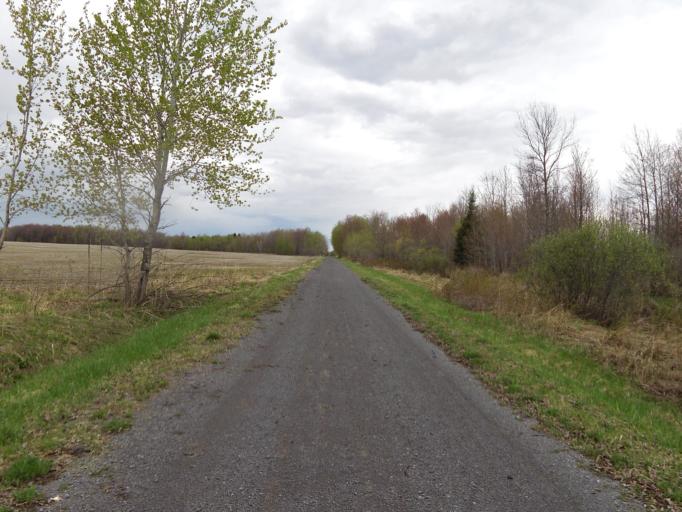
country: CA
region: Quebec
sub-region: Outaouais
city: Papineauville
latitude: 45.5180
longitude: -74.9532
